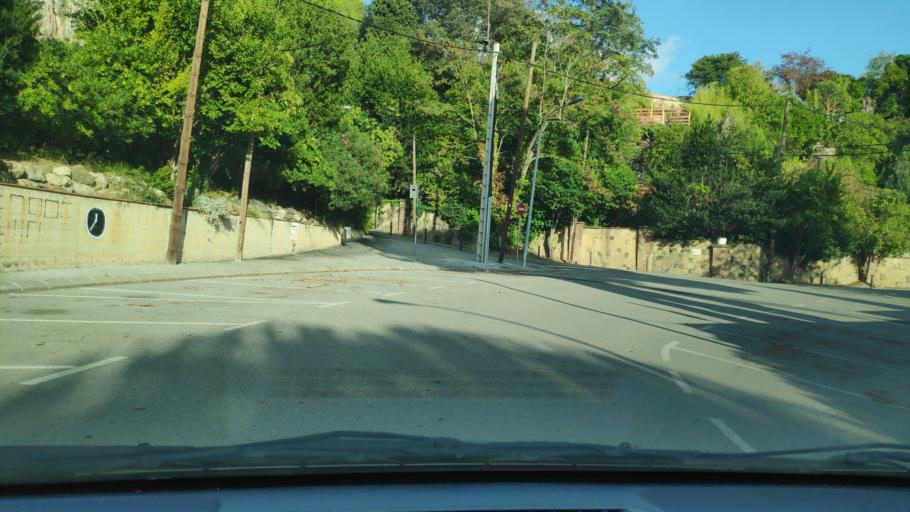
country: ES
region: Catalonia
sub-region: Provincia de Barcelona
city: Sant Quirze del Valles
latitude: 41.5045
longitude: 2.0825
